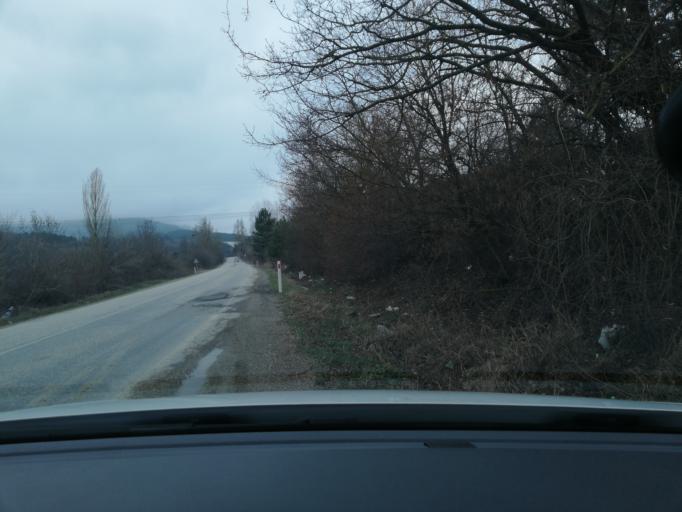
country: TR
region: Bolu
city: Bolu
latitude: 40.6844
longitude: 31.5316
